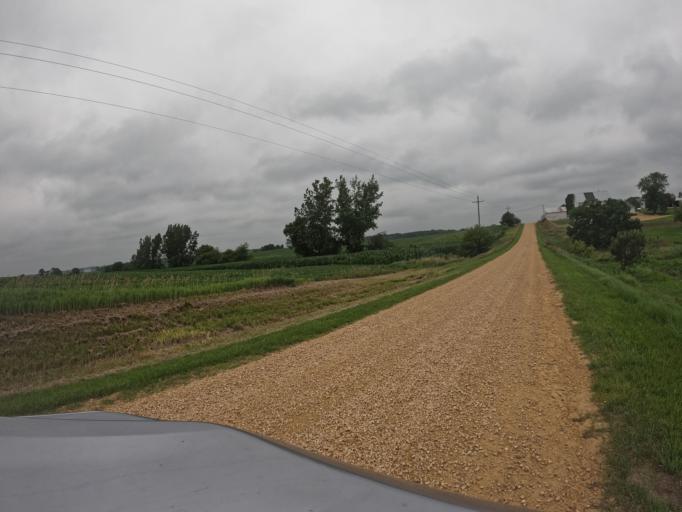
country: US
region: Iowa
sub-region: Clinton County
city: De Witt
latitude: 41.8910
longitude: -90.5783
